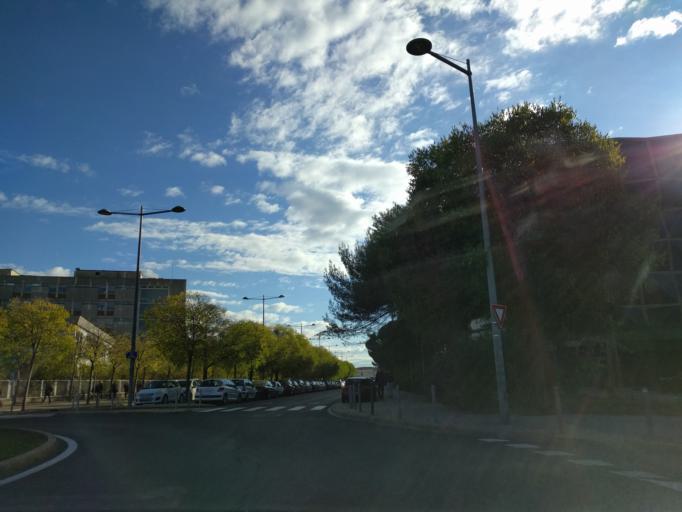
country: FR
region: Languedoc-Roussillon
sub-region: Departement de l'Herault
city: Montpellier
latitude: 43.6310
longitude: 3.8609
